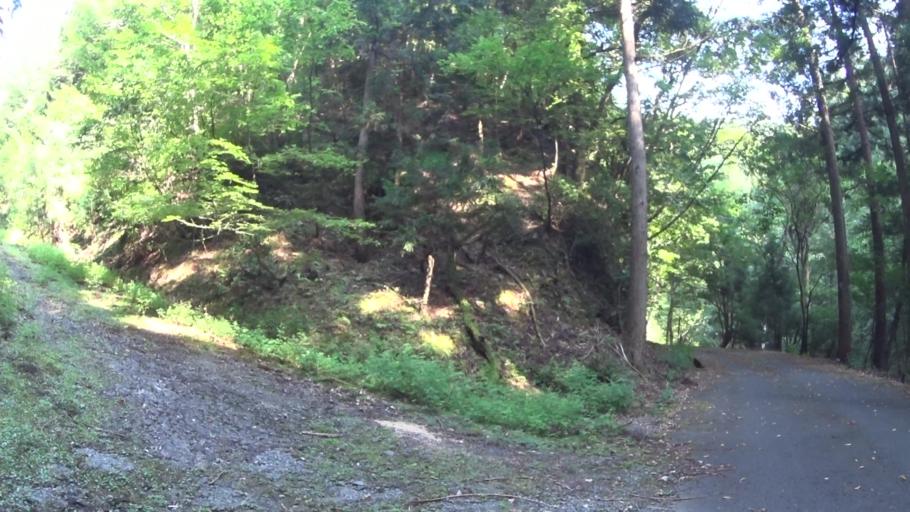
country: JP
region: Fukui
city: Obama
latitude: 35.2680
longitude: 135.6965
